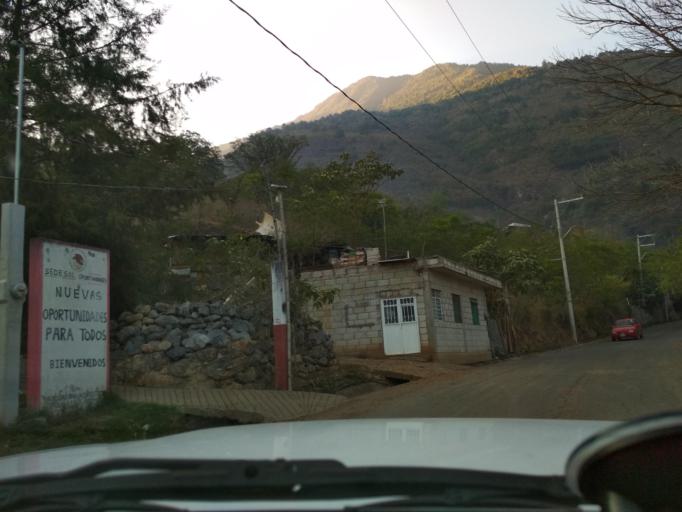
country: MX
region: Veracruz
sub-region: Nogales
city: Taza de Agua Ojo Zarco
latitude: 18.7732
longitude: -97.1947
